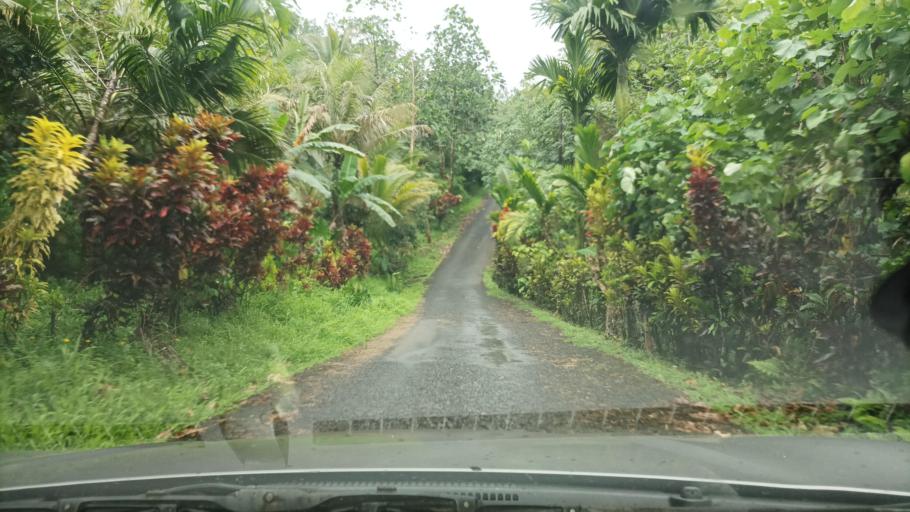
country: FM
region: Pohnpei
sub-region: Sokehs Municipality
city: Palikir - National Government Center
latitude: 6.8453
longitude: 158.1781
